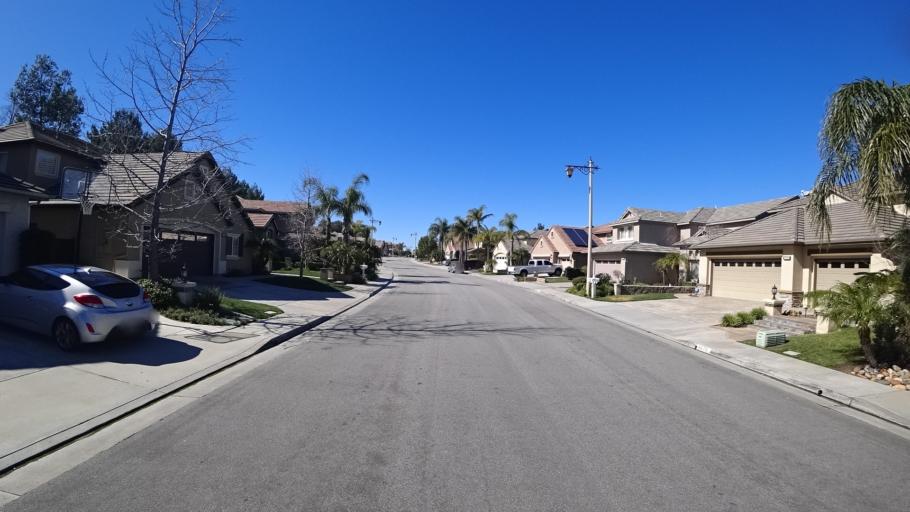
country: US
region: California
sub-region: Orange County
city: Yorba Linda
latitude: 33.8582
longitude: -117.7207
